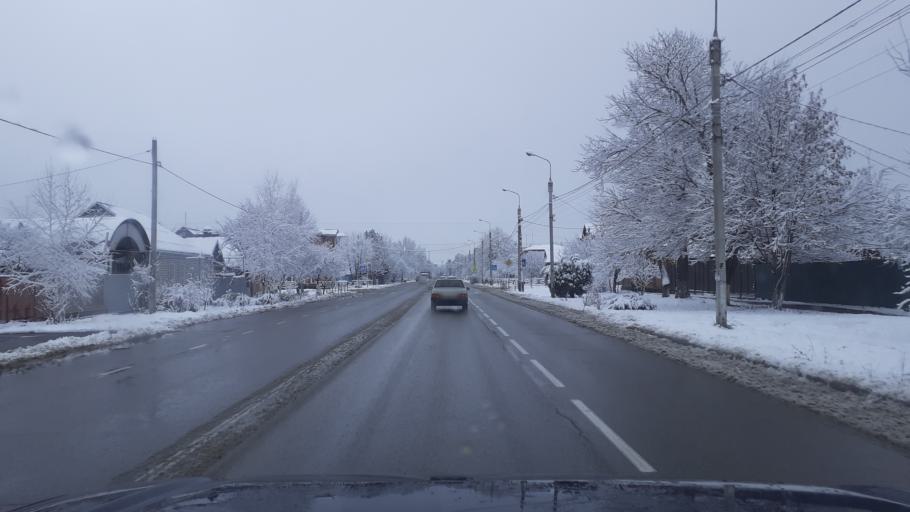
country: RU
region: Adygeya
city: Maykop
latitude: 44.6128
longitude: 40.1129
